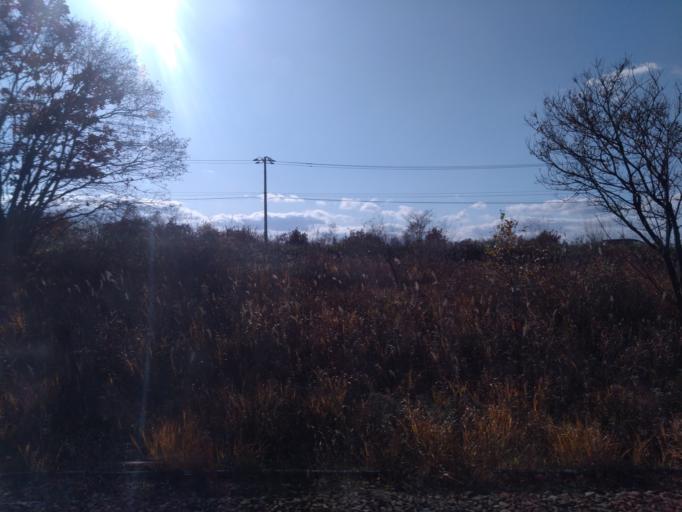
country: JP
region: Hokkaido
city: Chitose
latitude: 42.7907
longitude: 141.6958
